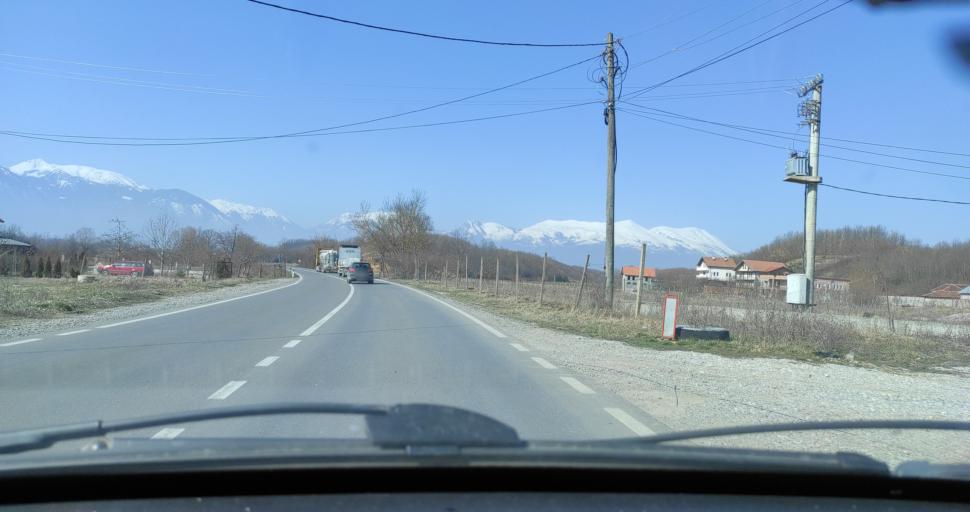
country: XK
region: Pec
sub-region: Komuna e Pejes
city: Kosuriq
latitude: 42.6365
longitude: 20.4445
